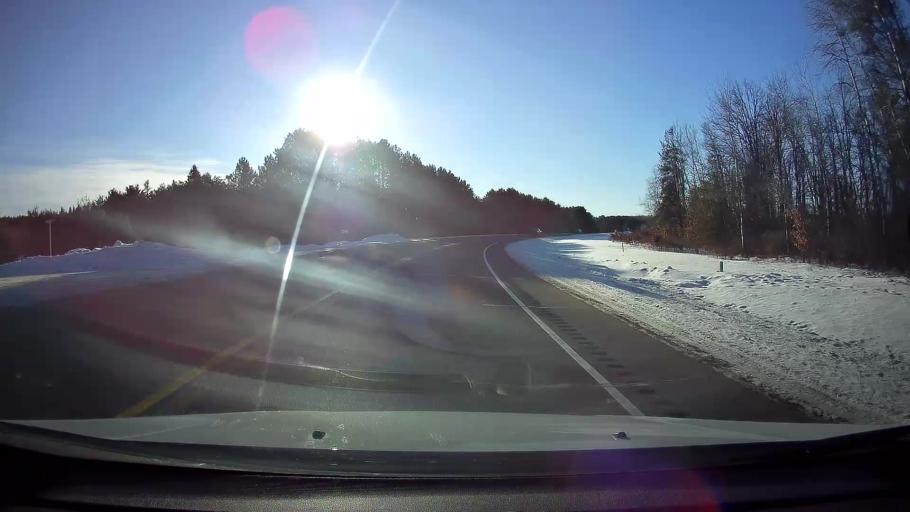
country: US
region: Wisconsin
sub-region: Sawyer County
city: Hayward
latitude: 45.9944
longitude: -91.5938
